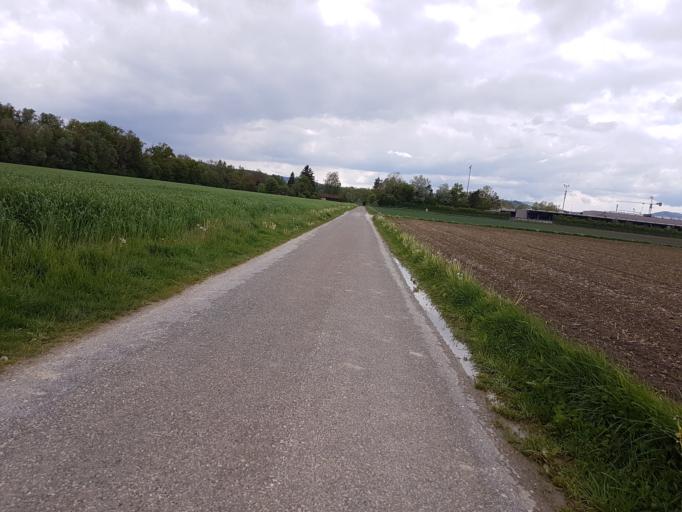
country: CH
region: Aargau
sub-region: Bezirk Brugg
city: Lauffohr (Brugg)
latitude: 47.4944
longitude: 8.2332
